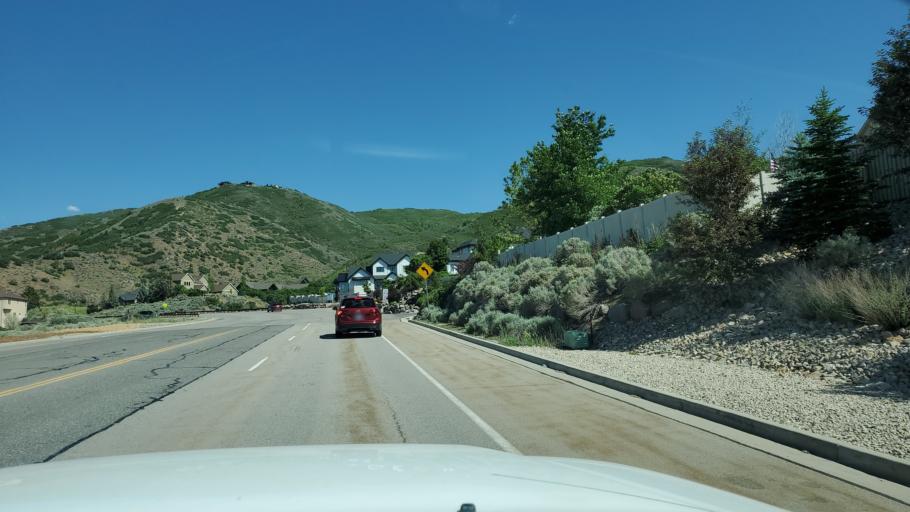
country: US
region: Utah
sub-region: Salt Lake County
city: Draper
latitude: 40.4850
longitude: -111.8681
